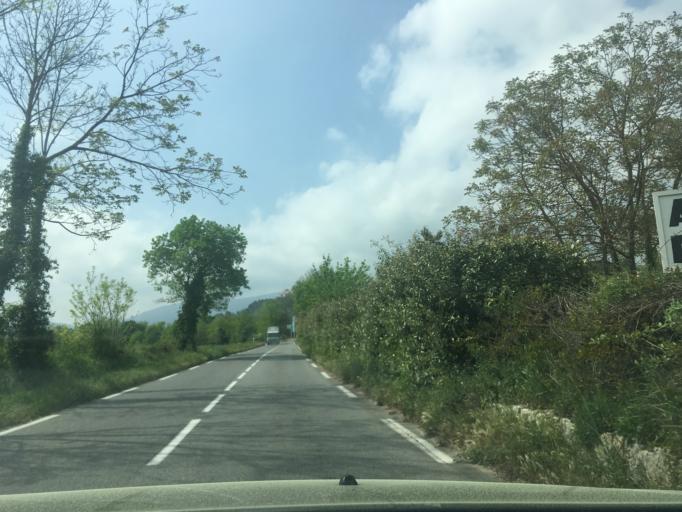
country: FR
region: Provence-Alpes-Cote d'Azur
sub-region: Departement du Var
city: Fayence
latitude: 43.6167
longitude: 6.7148
